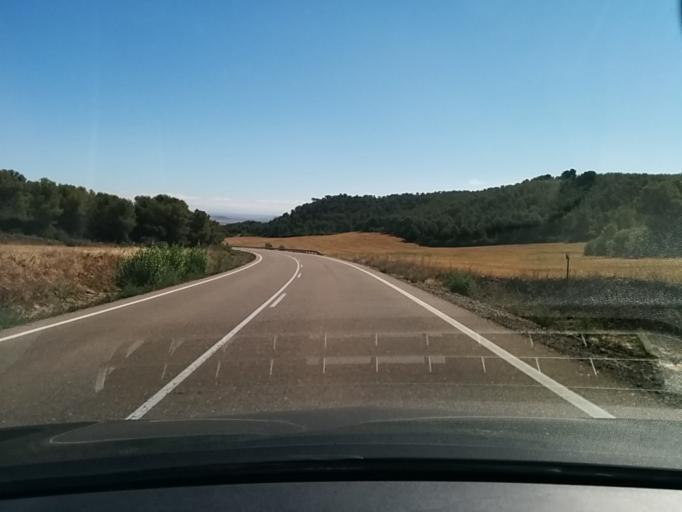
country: ES
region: Aragon
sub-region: Provincia de Huesca
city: Gurrea de Gallego
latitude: 42.0062
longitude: -0.8197
